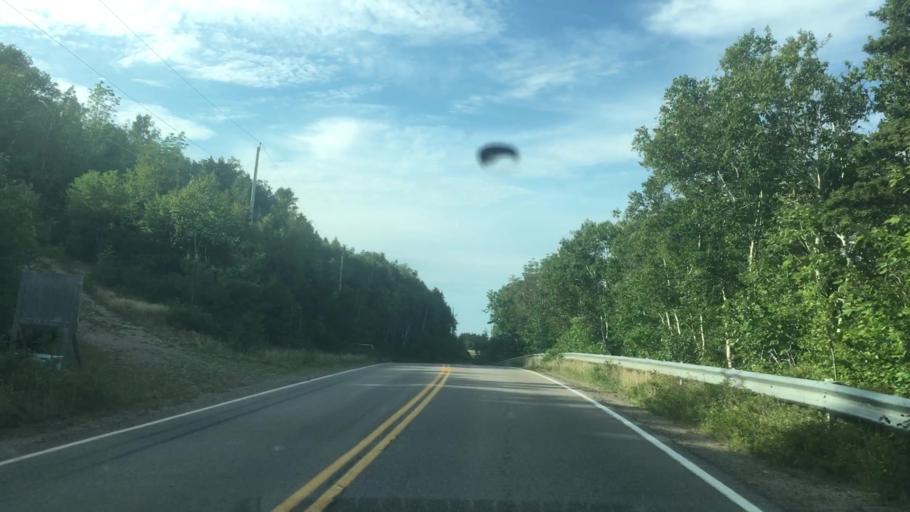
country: CA
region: Nova Scotia
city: Sydney Mines
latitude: 46.8245
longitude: -60.8005
